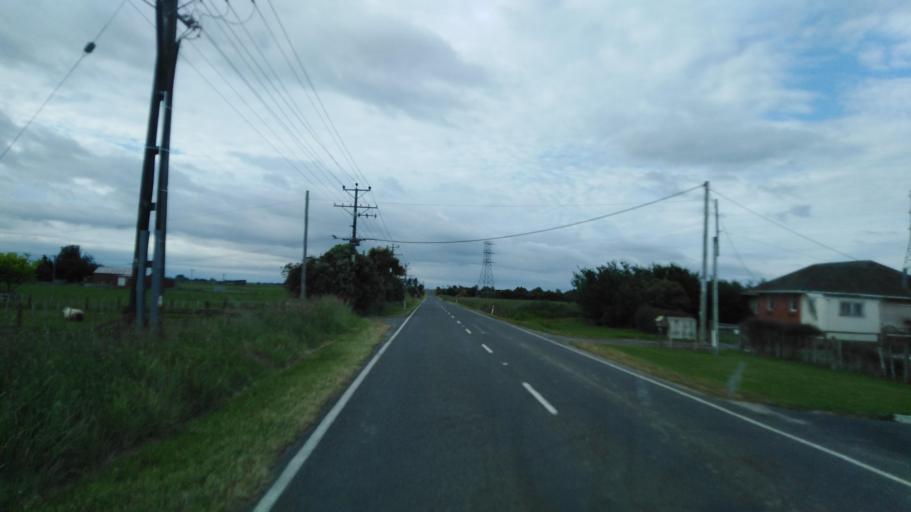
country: NZ
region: Manawatu-Wanganui
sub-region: Rangitikei District
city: Bulls
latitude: -40.1034
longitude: 175.3612
